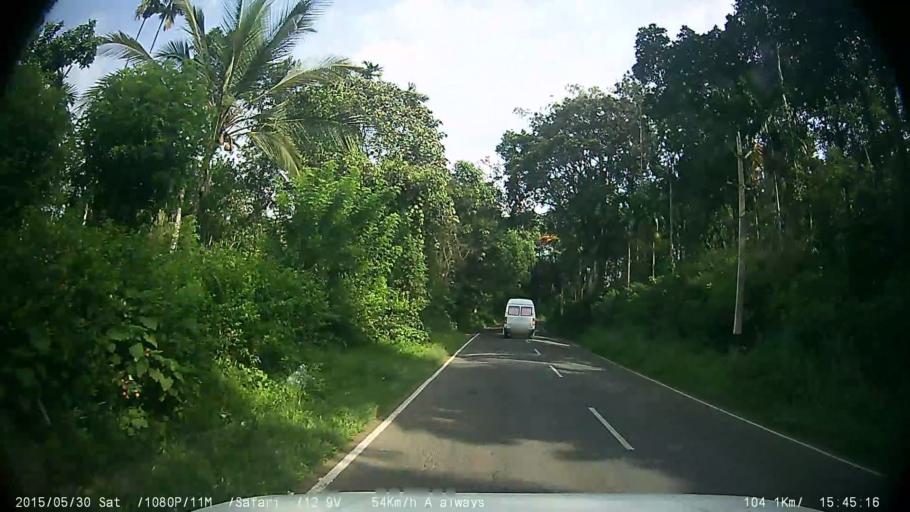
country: IN
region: Kerala
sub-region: Wayanad
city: Panamaram
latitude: 11.7188
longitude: 76.0802
